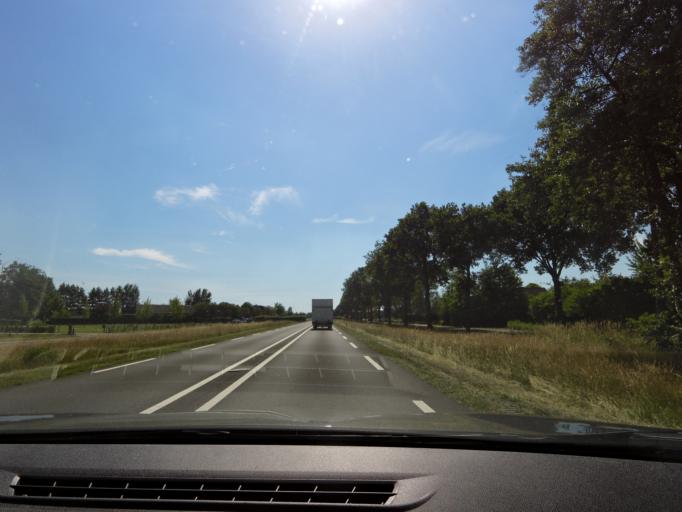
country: NL
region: Gelderland
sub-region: Oude IJsselstreek
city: Varsseveld
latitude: 51.9596
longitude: 6.4925
